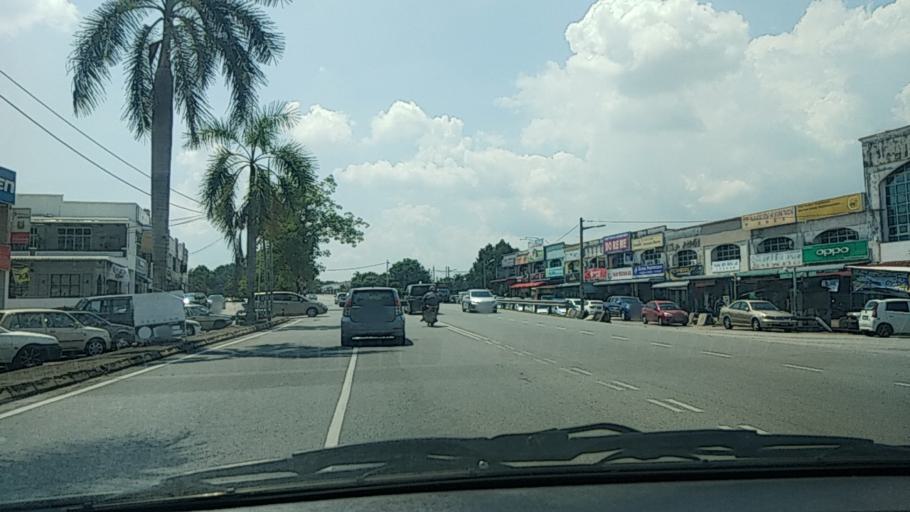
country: MY
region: Kedah
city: Sungai Petani
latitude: 5.6411
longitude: 100.5041
